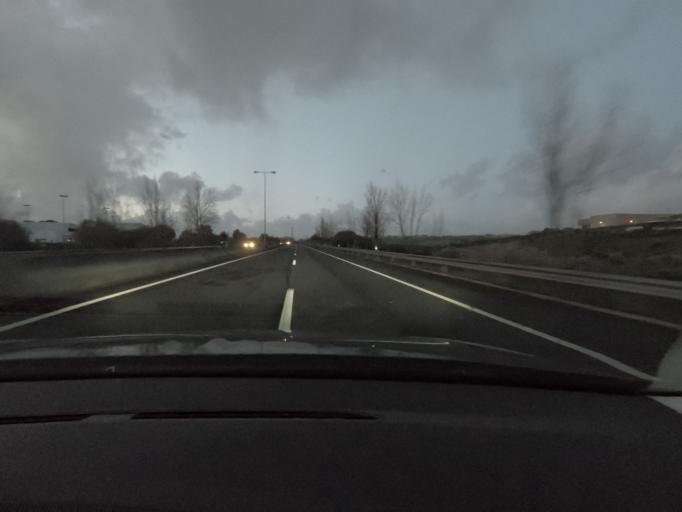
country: PT
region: Lisbon
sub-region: Oeiras
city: Porto Salvo
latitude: 38.7212
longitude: -9.2962
